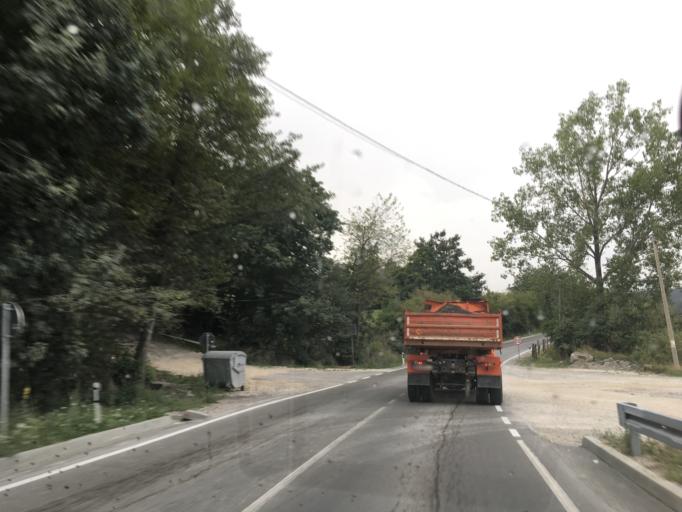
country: RS
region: Central Serbia
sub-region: Moravicki Okrug
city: Gornji Milanovac
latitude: 44.1309
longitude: 20.4946
